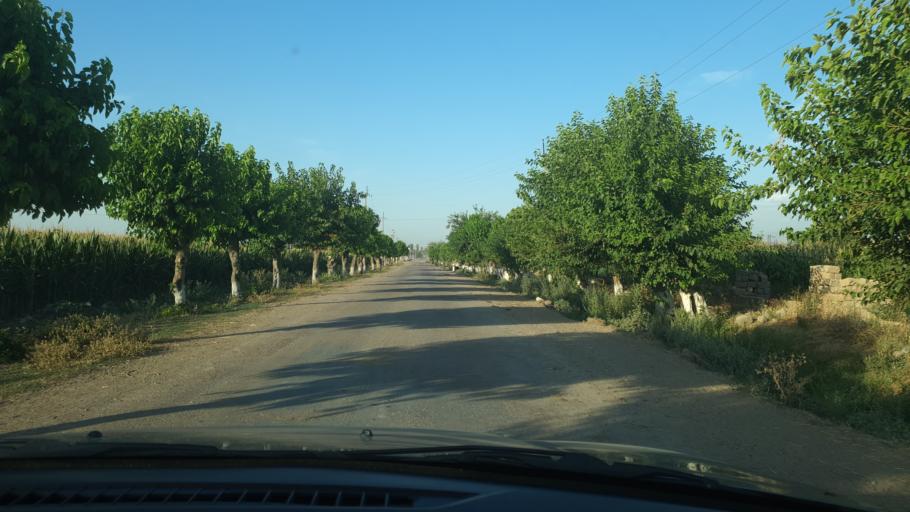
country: UZ
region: Toshkent
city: Tuytepa
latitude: 41.1014
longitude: 69.3836
